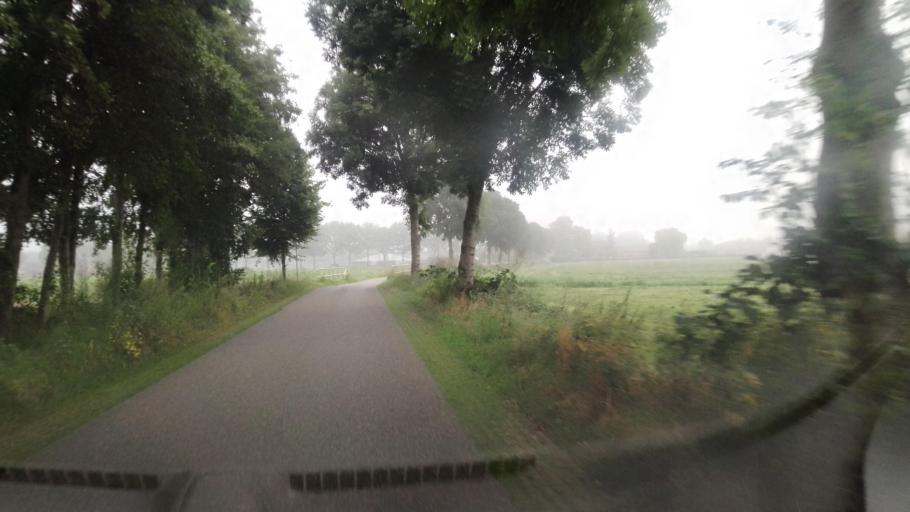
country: NL
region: Limburg
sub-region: Gemeente Peel en Maas
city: Maasbree
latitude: 51.4261
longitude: 6.0291
